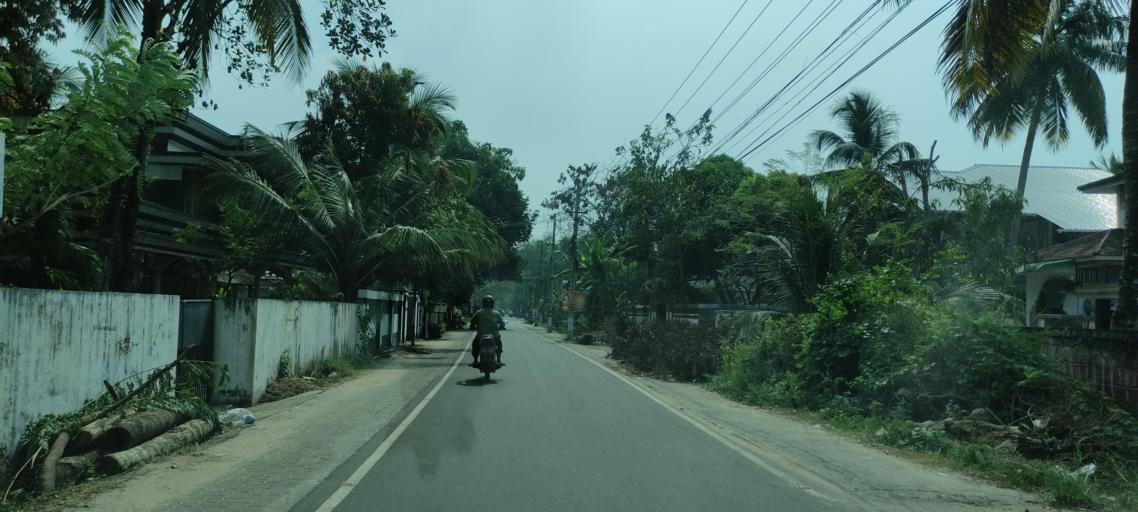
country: IN
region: Kerala
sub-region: Alappuzha
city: Alleppey
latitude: 9.5142
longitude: 76.3343
